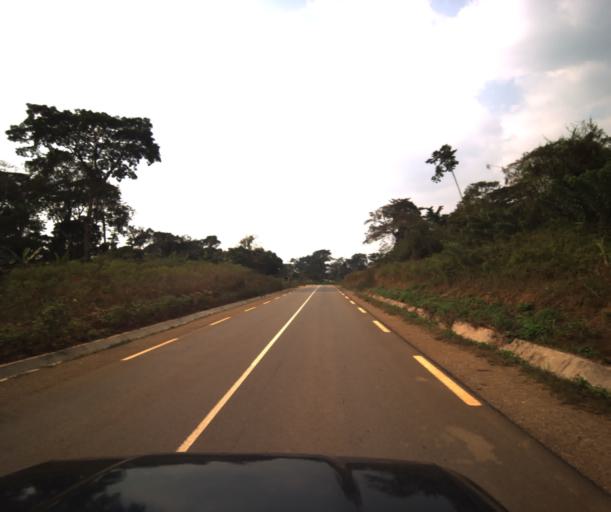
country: CM
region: Centre
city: Mbankomo
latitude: 3.7397
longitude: 11.3944
